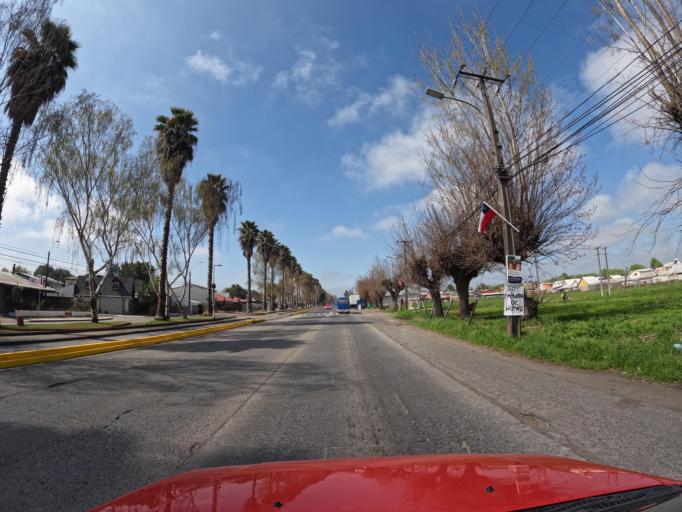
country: CL
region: Maule
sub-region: Provincia de Curico
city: Molina
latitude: -35.0518
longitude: -71.2788
